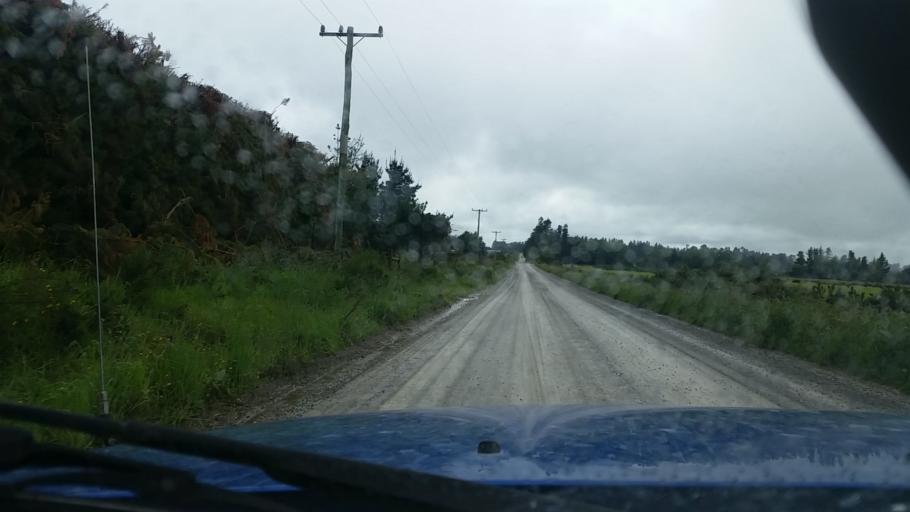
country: NZ
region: Canterbury
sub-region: Ashburton District
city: Methven
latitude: -43.6092
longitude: 171.4759
